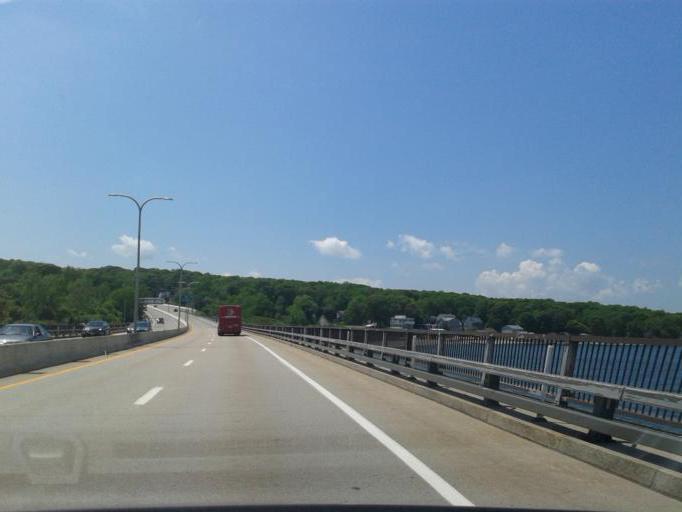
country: US
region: Rhode Island
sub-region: Washington County
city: North Kingstown
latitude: 41.5302
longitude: -71.4142
